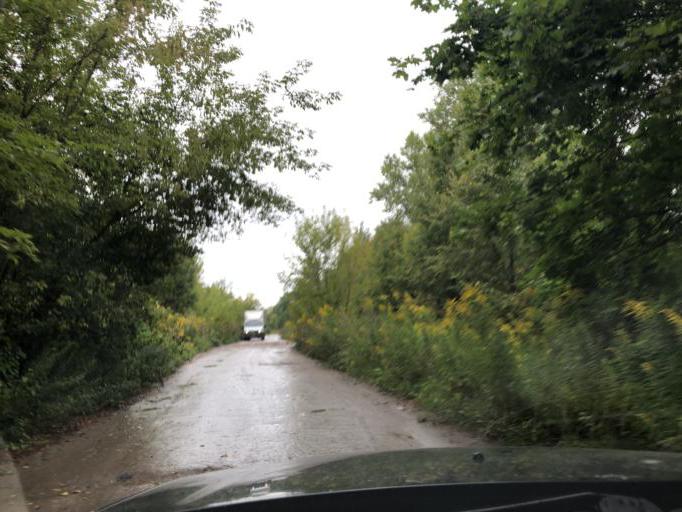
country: RU
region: Tula
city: Mendeleyevskiy
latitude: 54.1698
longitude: 37.5520
